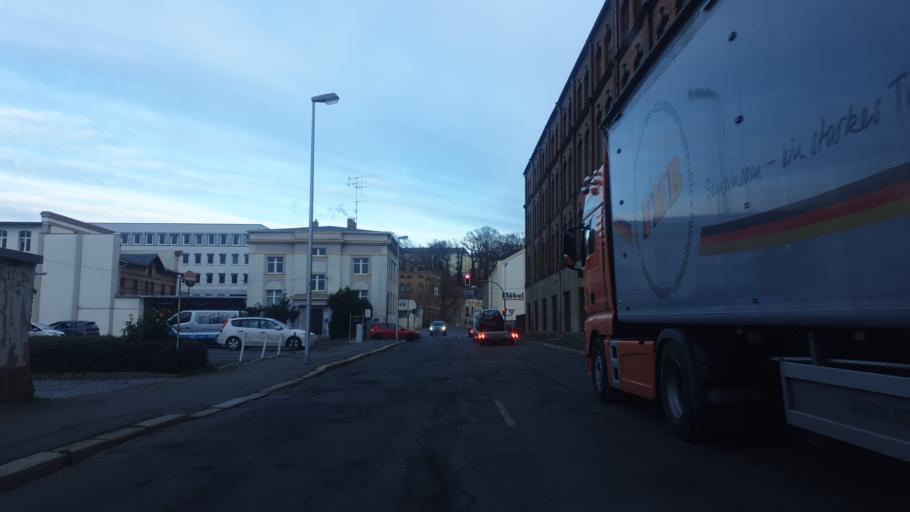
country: DE
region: Thuringia
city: Gera
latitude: 50.8694
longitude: 12.0826
